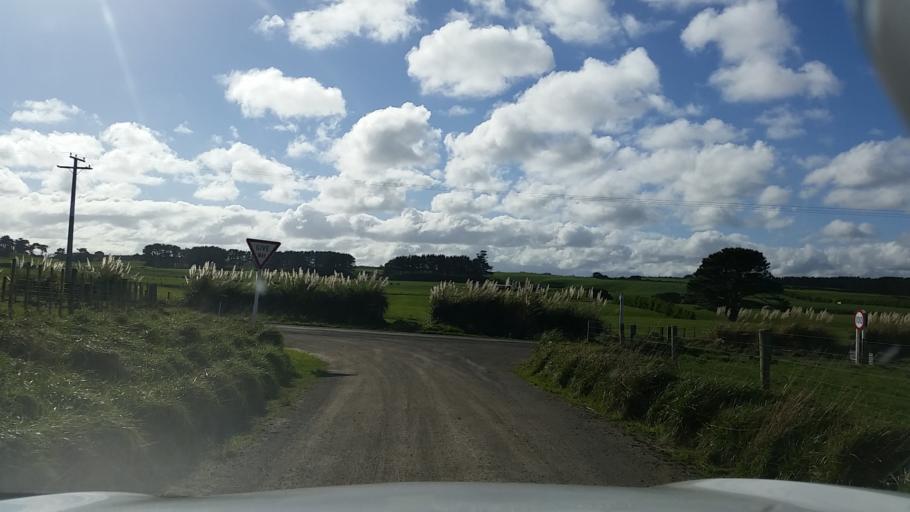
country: NZ
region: Taranaki
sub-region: South Taranaki District
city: Patea
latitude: -39.7116
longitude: 174.4548
